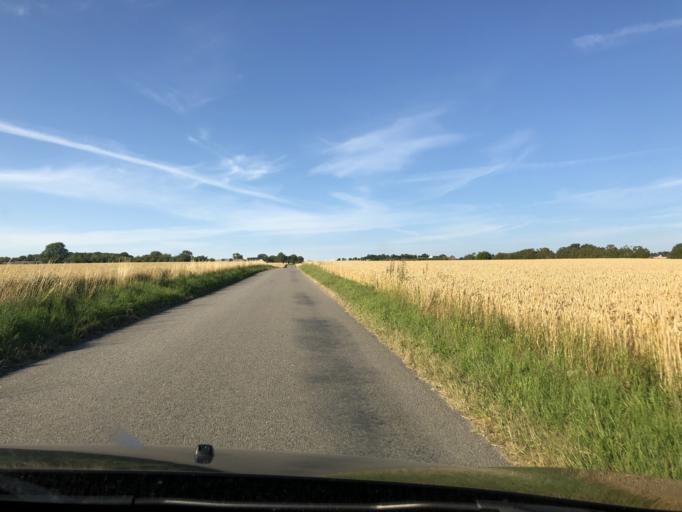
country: DK
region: South Denmark
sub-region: AEro Kommune
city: AEroskobing
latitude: 54.8597
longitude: 10.3655
